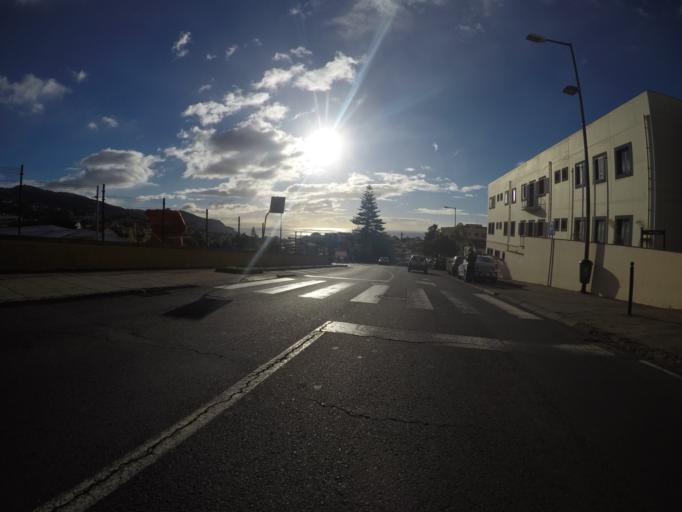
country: PT
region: Madeira
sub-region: Funchal
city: Nossa Senhora do Monte
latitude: 32.6643
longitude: -16.9358
